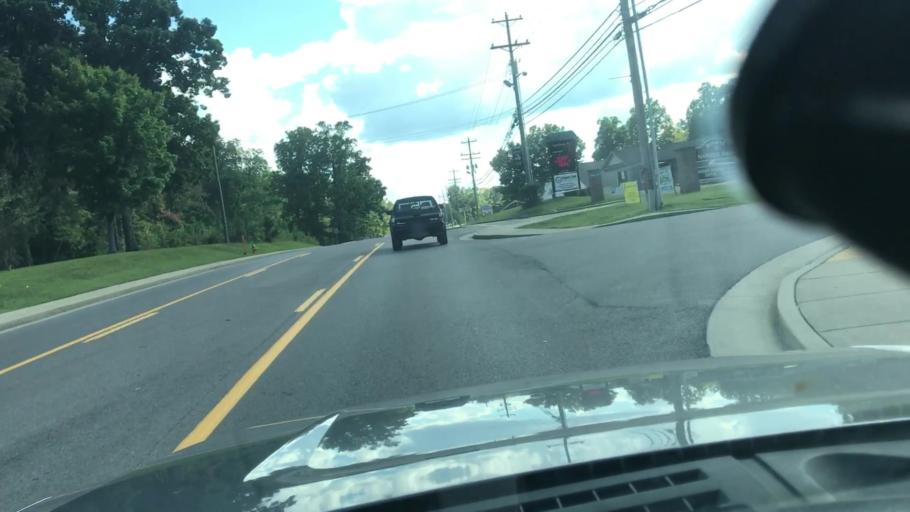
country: US
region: Tennessee
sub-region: Williamson County
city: Fairview
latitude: 35.9697
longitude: -87.1308
